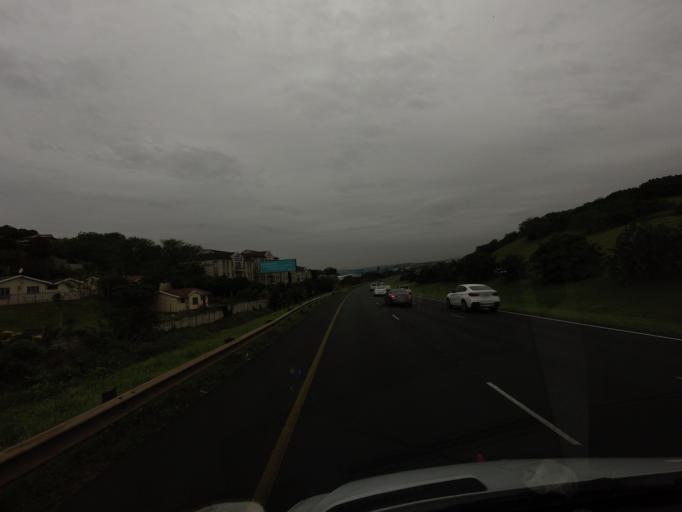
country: ZA
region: KwaZulu-Natal
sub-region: eThekwini Metropolitan Municipality
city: Durban
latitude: -29.7466
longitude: 31.0373
